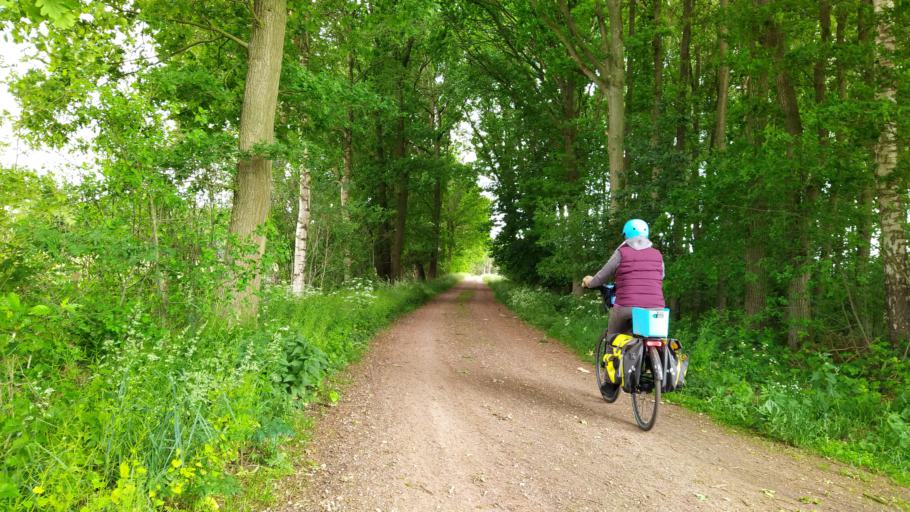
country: DE
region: Lower Saxony
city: Farven
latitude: 53.4316
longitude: 9.2764
